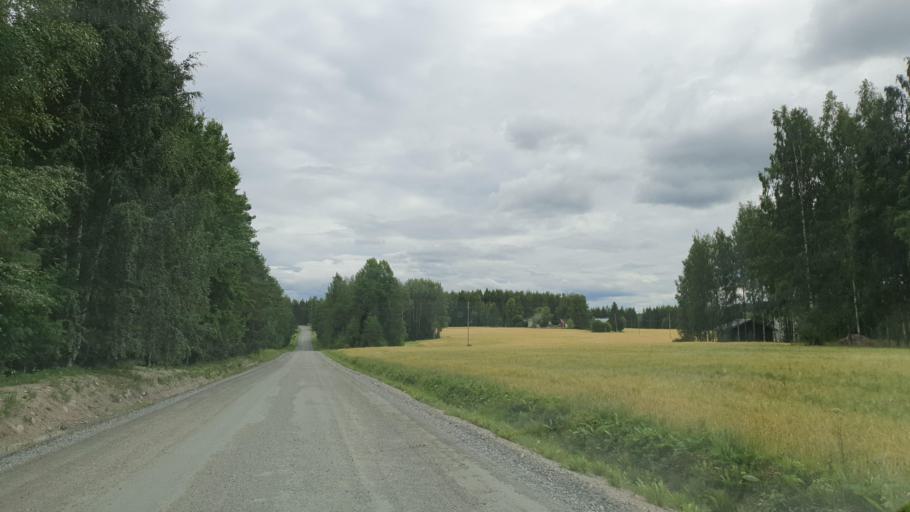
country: FI
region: Northern Savo
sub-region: Ylae-Savo
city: Iisalmi
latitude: 63.5229
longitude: 27.0947
